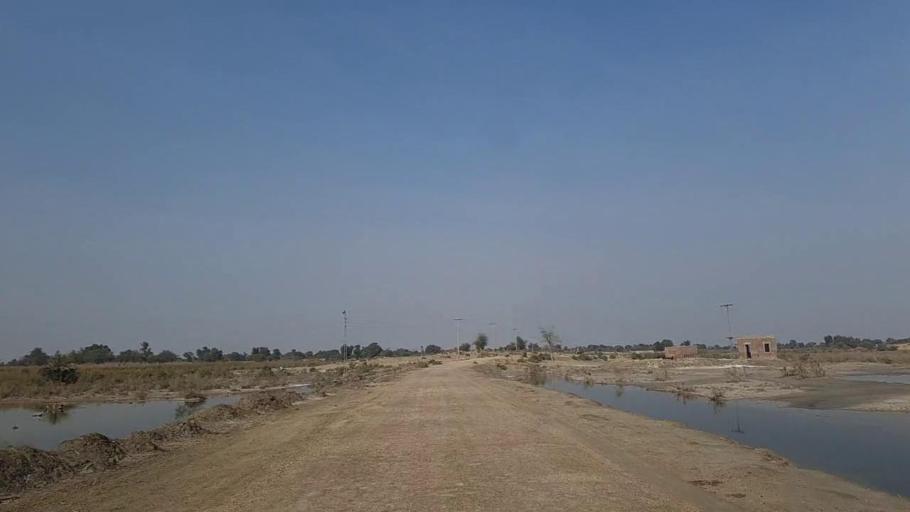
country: PK
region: Sindh
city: Daur
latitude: 26.5090
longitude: 68.4795
